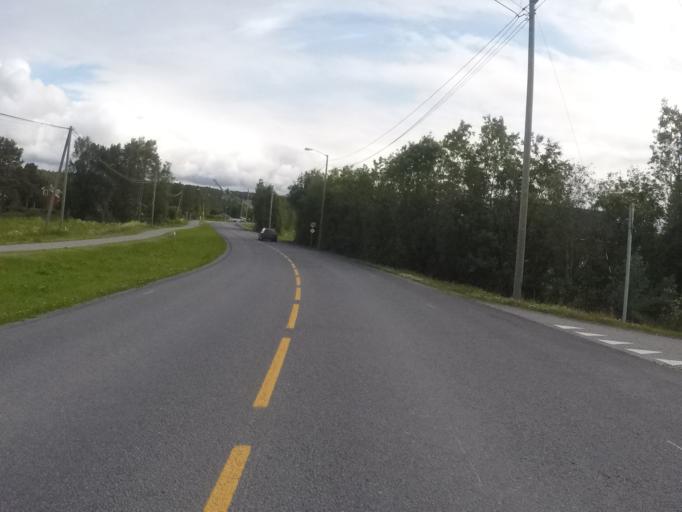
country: NO
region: Finnmark Fylke
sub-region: Alta
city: Alta
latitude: 69.9626
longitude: 23.3151
